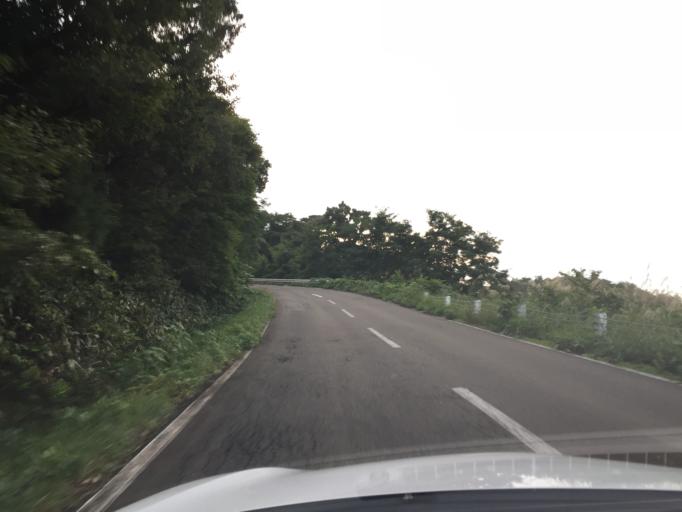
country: JP
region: Fukushima
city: Kitakata
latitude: 37.5694
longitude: 139.9475
